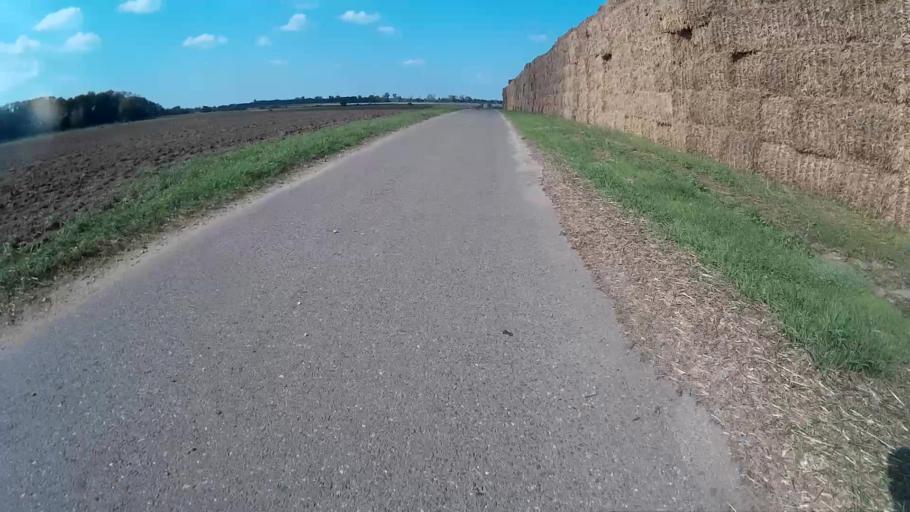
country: CZ
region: South Moravian
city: Hrusovany nad Jevisovkou
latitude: 48.8041
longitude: 16.4273
